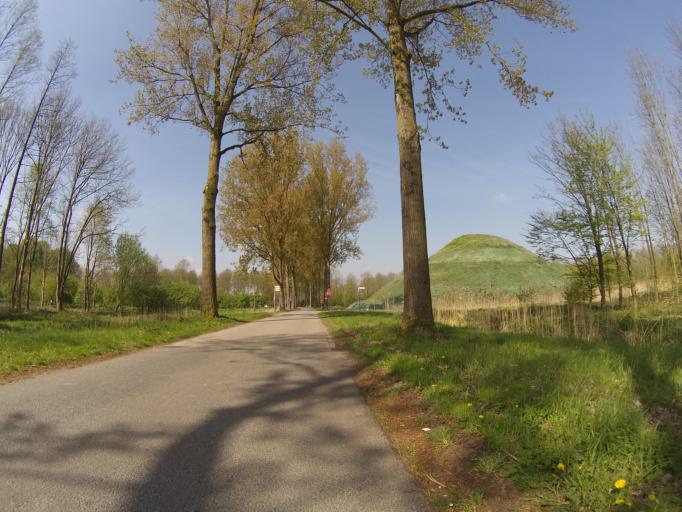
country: NL
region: North Holland
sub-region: Gemeente Huizen
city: Huizen
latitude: 52.3226
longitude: 5.2923
